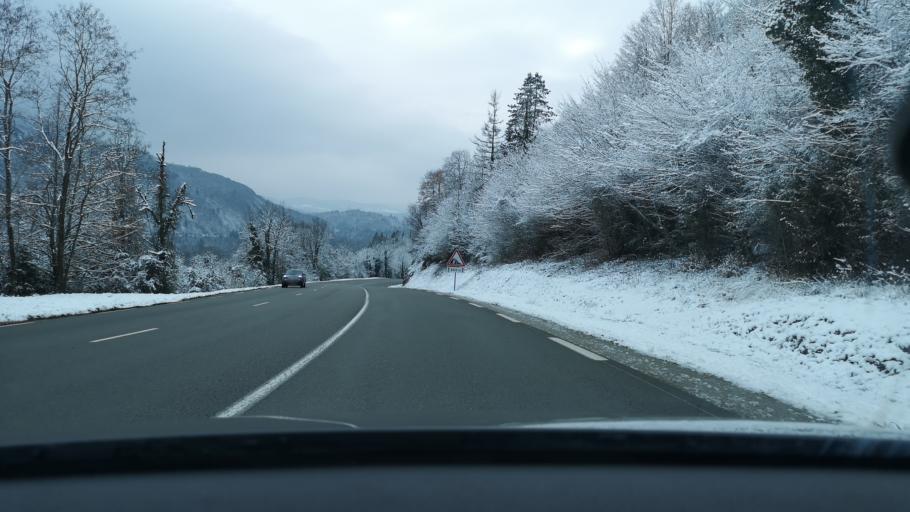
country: FR
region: Franche-Comte
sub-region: Departement du Jura
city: Moirans-en-Montagne
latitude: 46.3740
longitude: 5.7075
